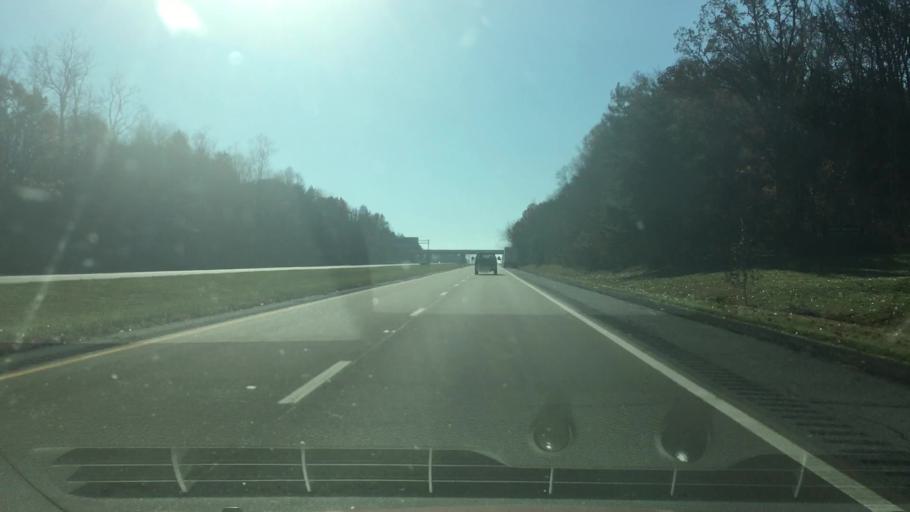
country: US
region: Ohio
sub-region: Wayne County
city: Wooster
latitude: 40.7799
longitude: -81.9145
